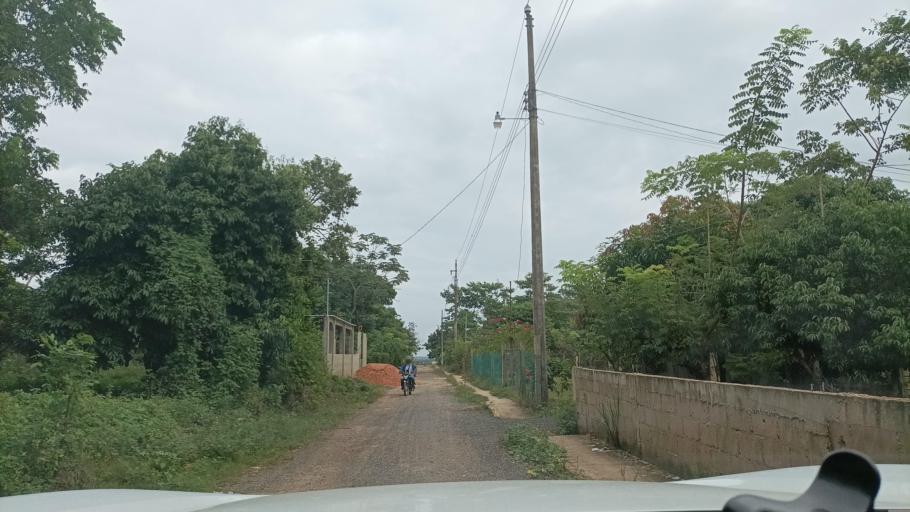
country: MX
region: Veracruz
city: Oteapan
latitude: 17.9883
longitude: -94.6742
